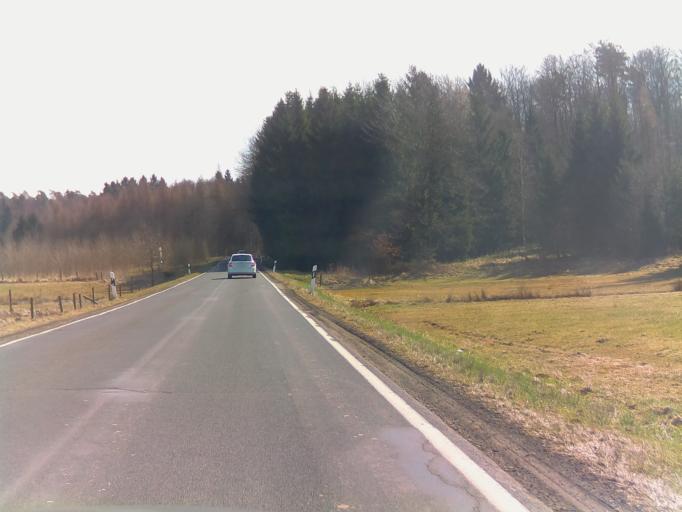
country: DE
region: Hesse
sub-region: Regierungsbezirk Giessen
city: Grunberg
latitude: 50.6303
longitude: 8.9959
